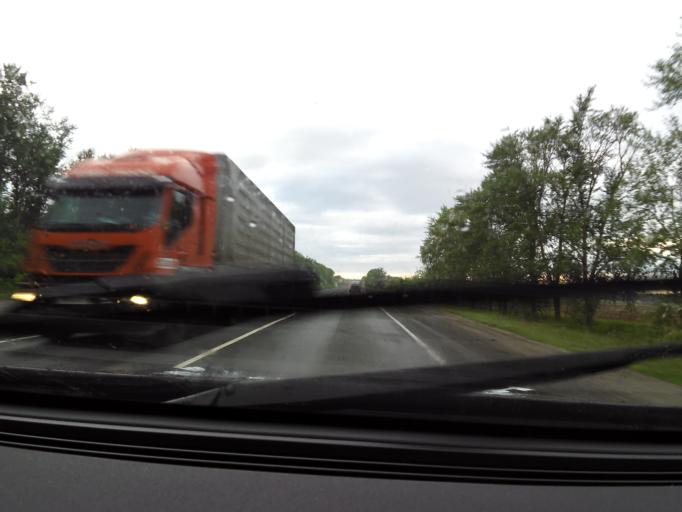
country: RU
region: Chuvashia
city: Yantikovo
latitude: 55.7894
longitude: 47.7107
